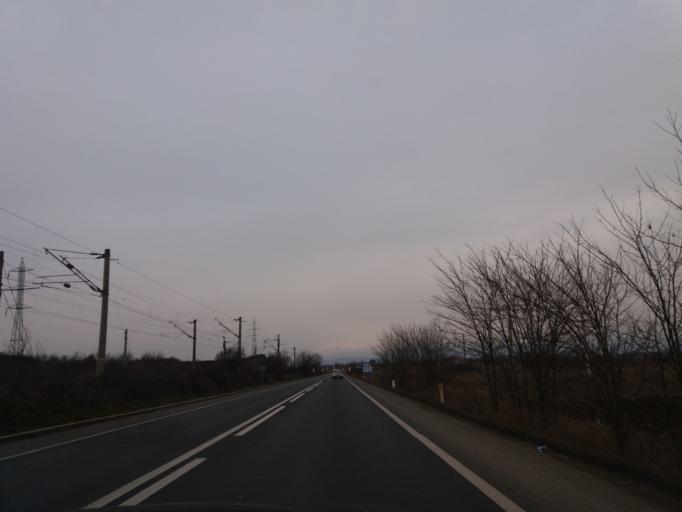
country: RO
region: Hunedoara
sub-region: Comuna Calan
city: Calan
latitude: 45.7652
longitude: 23.0001
